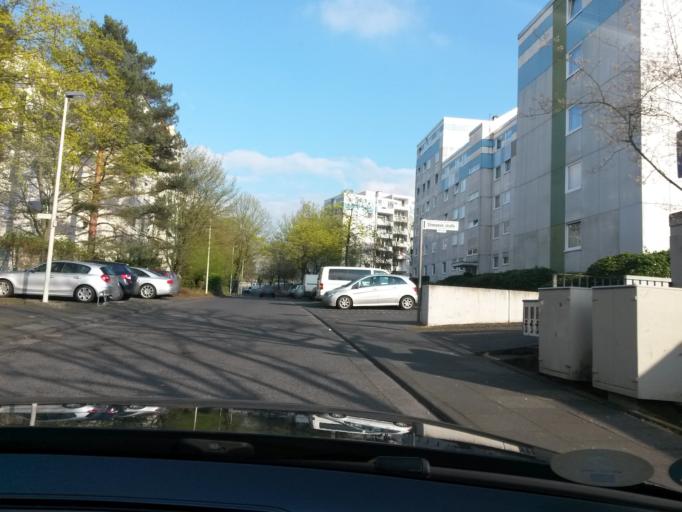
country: DE
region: North Rhine-Westphalia
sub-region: Regierungsbezirk Koln
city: Alfter
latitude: 50.7102
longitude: 7.0335
